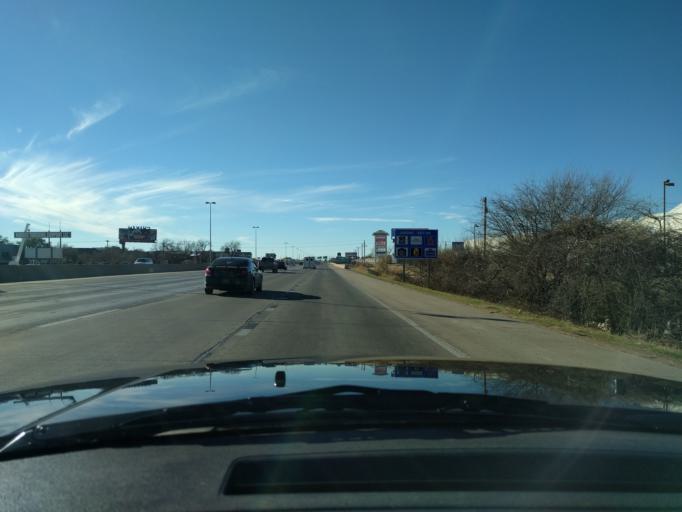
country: US
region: Oklahoma
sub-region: Oklahoma County
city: Warr Acres
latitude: 35.4603
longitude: -97.5899
